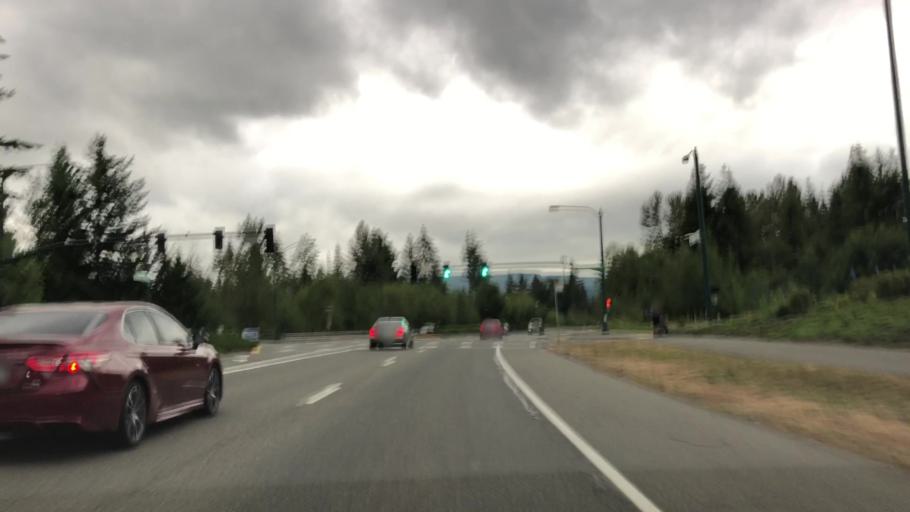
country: US
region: Washington
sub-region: King County
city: Fall City
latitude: 47.5169
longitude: -121.8793
